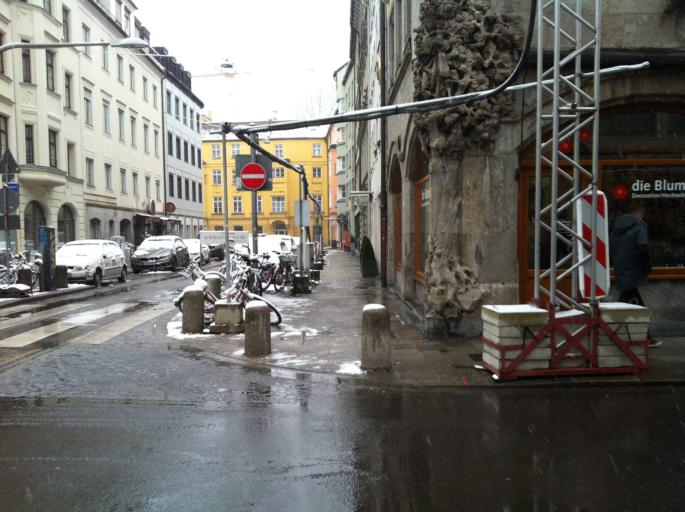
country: DE
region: Bavaria
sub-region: Upper Bavaria
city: Munich
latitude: 48.1364
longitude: 11.5684
